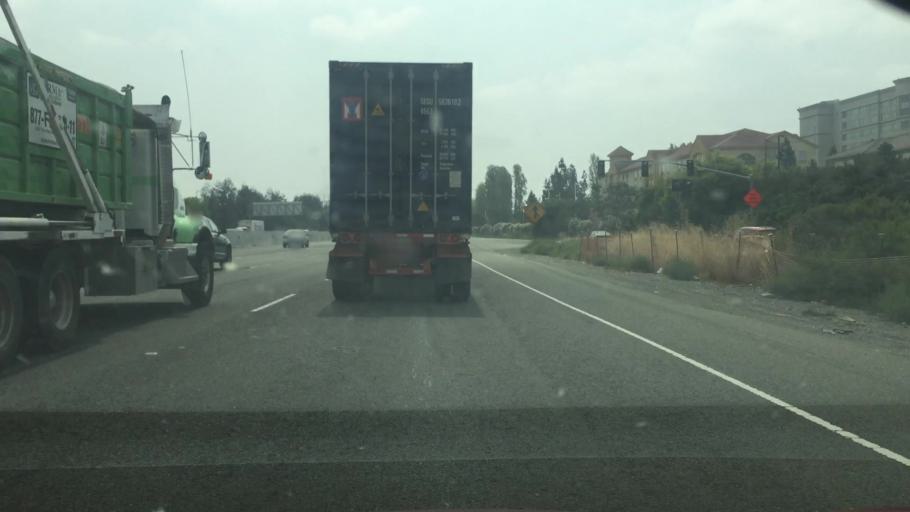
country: US
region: California
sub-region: Alameda County
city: Fremont
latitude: 37.4913
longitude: -121.9470
